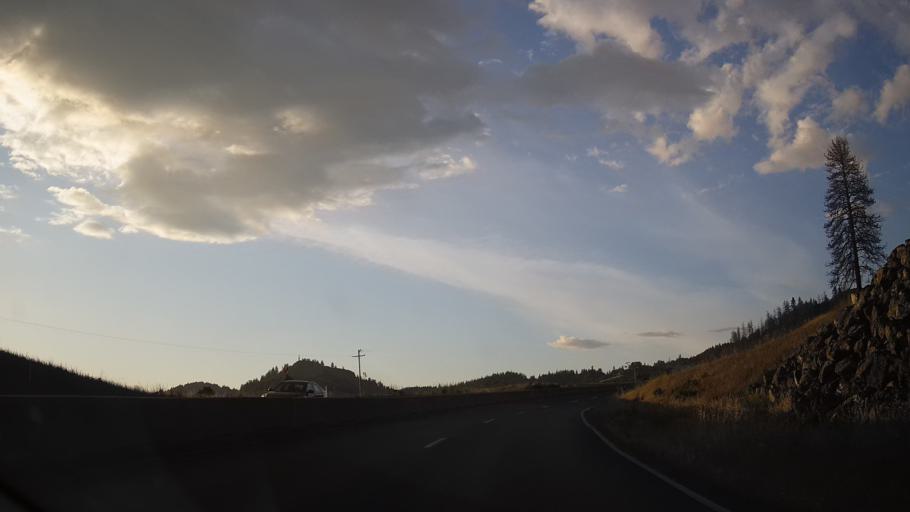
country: US
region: California
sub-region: Mendocino County
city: Willits
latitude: 39.3173
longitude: -123.3012
